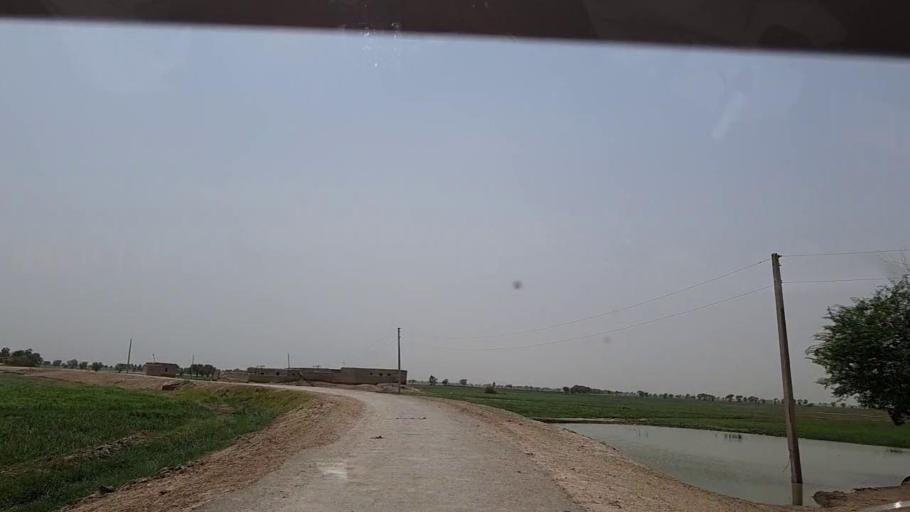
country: PK
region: Sindh
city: Khairpur Nathan Shah
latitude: 27.0094
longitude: 67.6553
